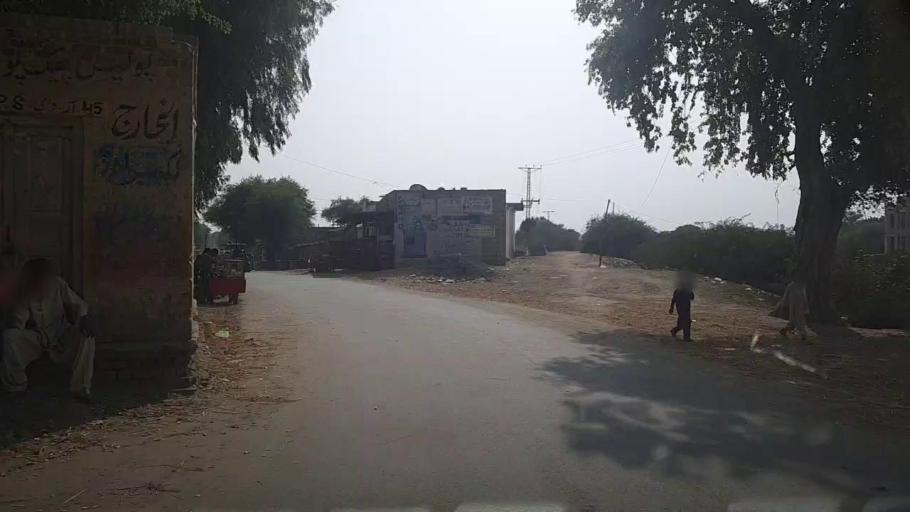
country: PK
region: Sindh
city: Kashmor
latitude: 28.4239
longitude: 69.5713
